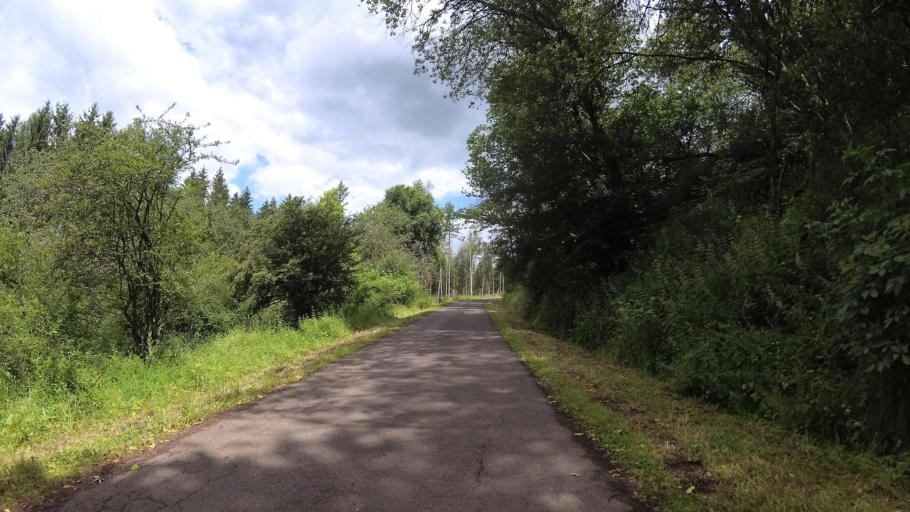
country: DE
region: Rheinland-Pfalz
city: Neuhutten
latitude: 49.5771
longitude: 7.0105
